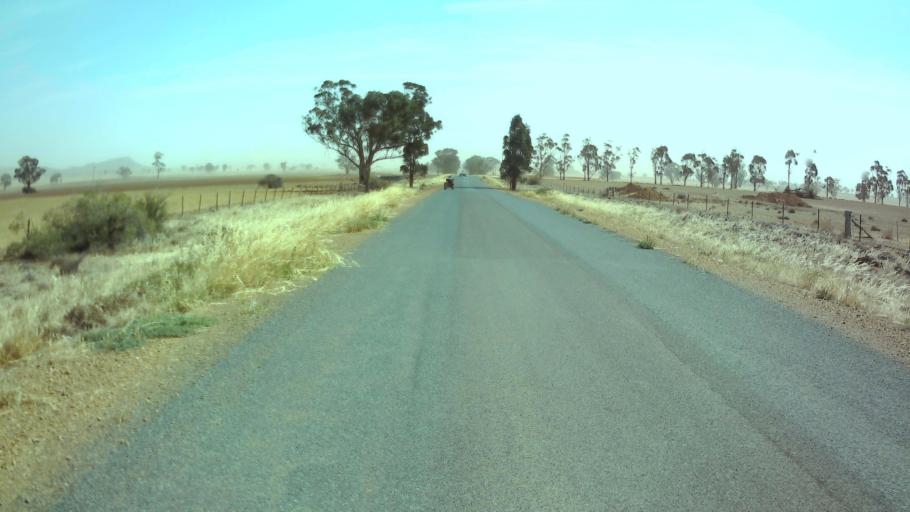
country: AU
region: New South Wales
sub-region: Weddin
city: Grenfell
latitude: -33.7673
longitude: 147.9875
